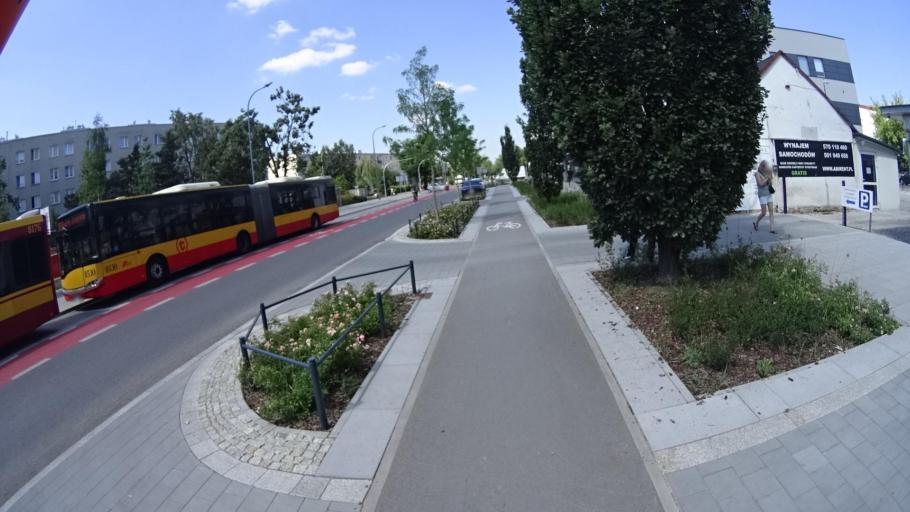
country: PL
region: Masovian Voivodeship
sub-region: Powiat piaseczynski
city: Piaseczno
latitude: 52.0770
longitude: 21.0263
